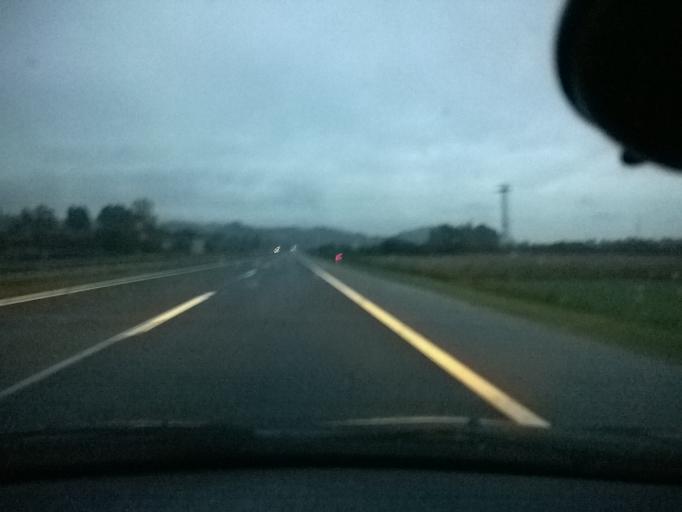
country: HR
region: Krapinsko-Zagorska
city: Zabok
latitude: 46.0488
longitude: 15.9223
